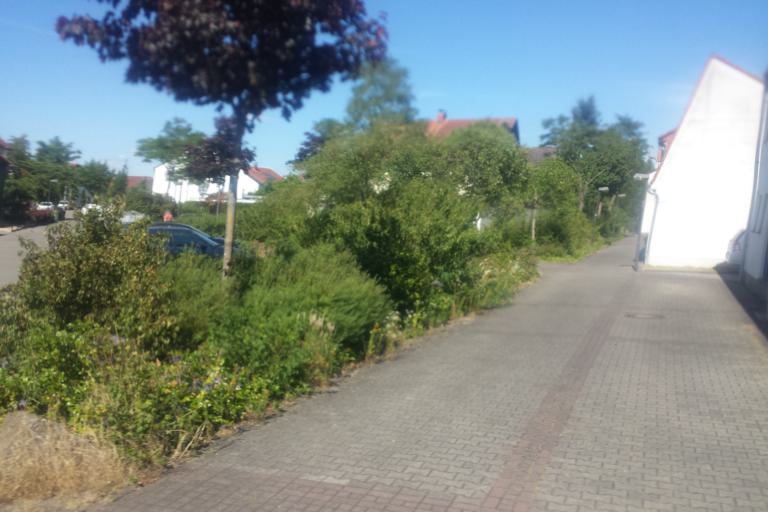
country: DE
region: Hesse
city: Lampertheim
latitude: 49.6002
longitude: 8.5100
